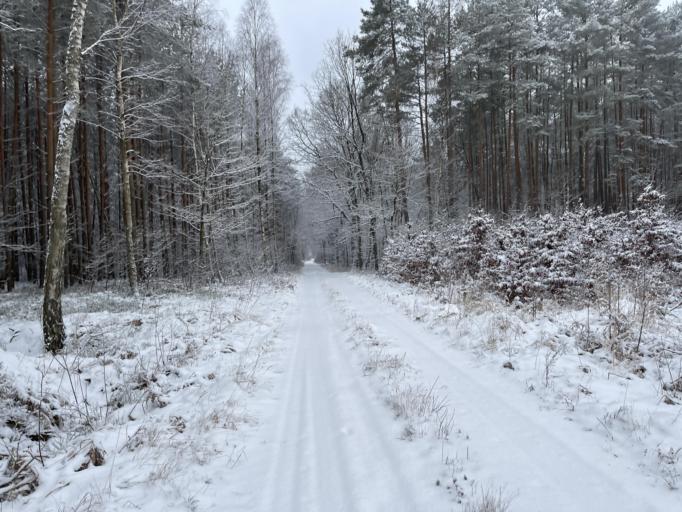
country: PL
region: Masovian Voivodeship
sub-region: Powiat zyrardowski
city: Mrozy
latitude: 52.0371
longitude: 20.2739
